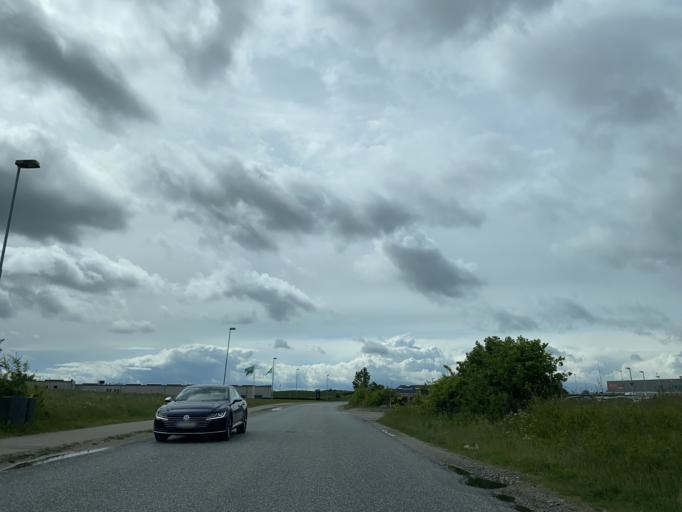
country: DK
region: Central Jutland
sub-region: Arhus Kommune
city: Stavtrup
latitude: 56.1858
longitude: 10.1291
